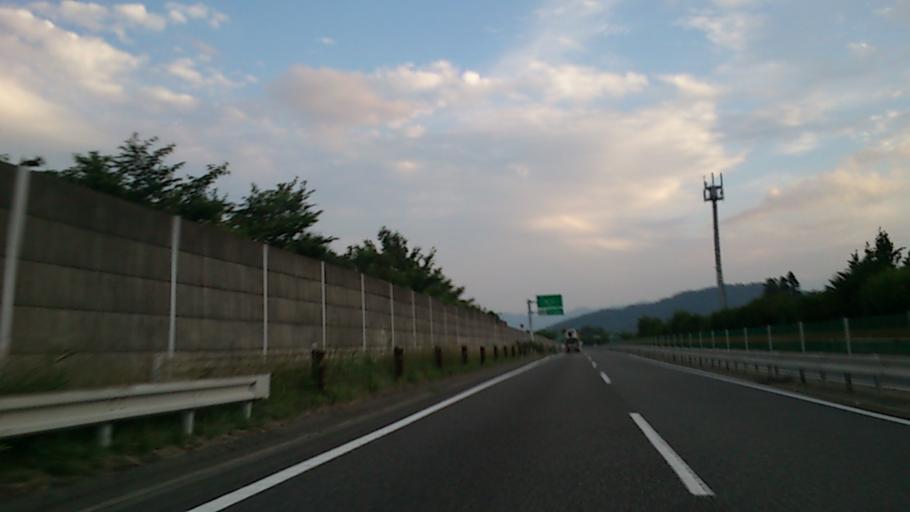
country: JP
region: Nagano
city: Iida
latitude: 35.5067
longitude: 137.7994
